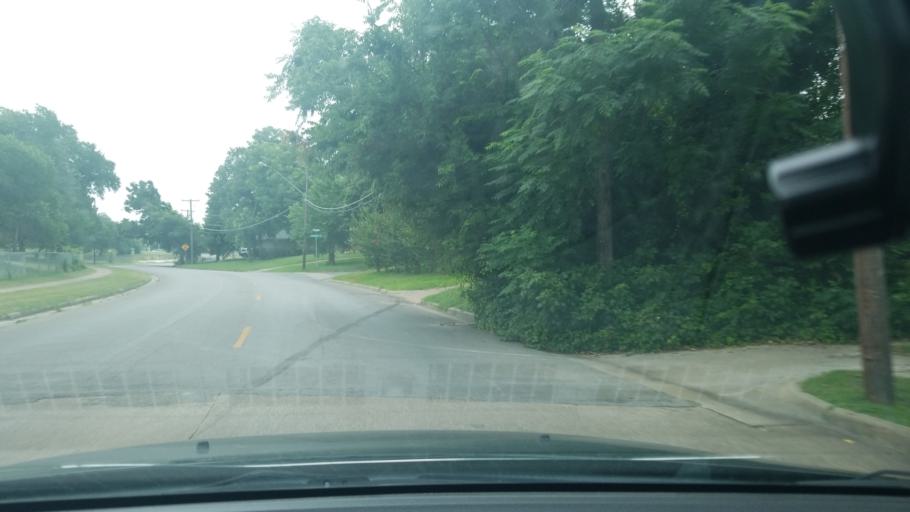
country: US
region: Texas
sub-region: Dallas County
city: Balch Springs
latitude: 32.7608
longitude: -96.6881
